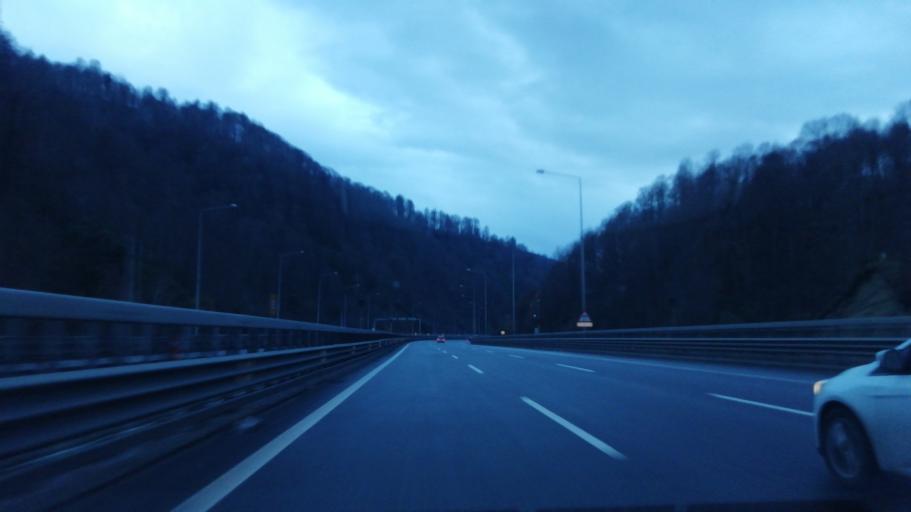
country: TR
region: Duzce
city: Kaynasli
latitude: 40.7582
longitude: 31.4413
